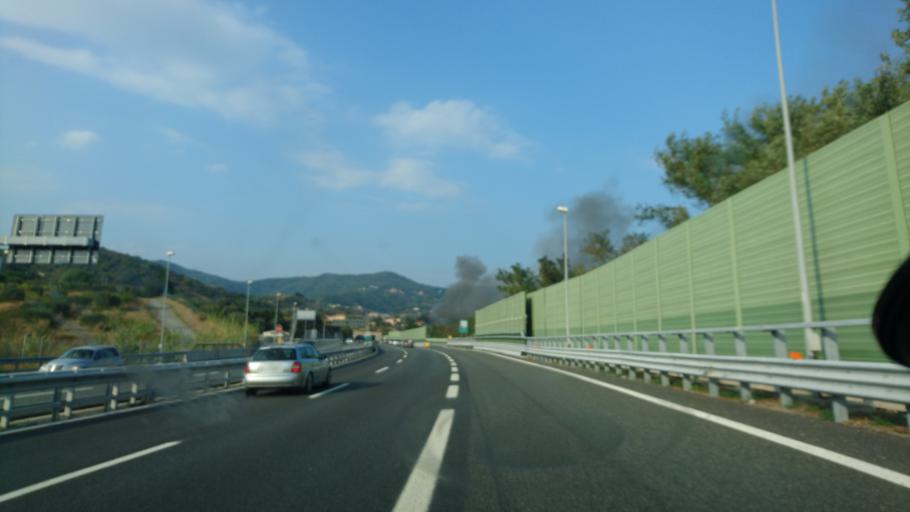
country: IT
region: Liguria
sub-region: Provincia di Savona
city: Valleggia
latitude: 44.2925
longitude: 8.4464
